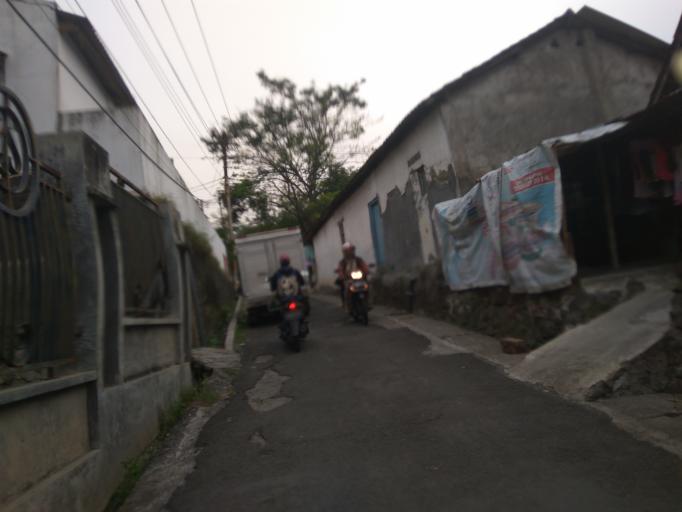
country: ID
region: Central Java
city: Semarang
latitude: -7.0135
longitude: 110.4110
